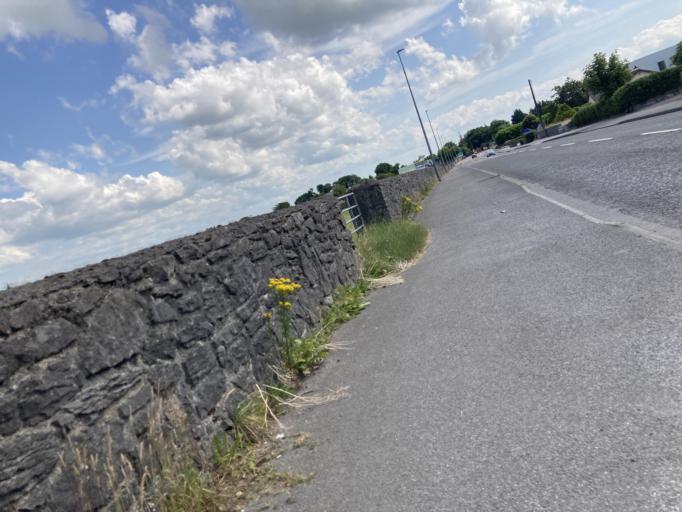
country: IE
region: Connaught
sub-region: County Galway
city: Claregalway
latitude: 53.2954
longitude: -8.9851
